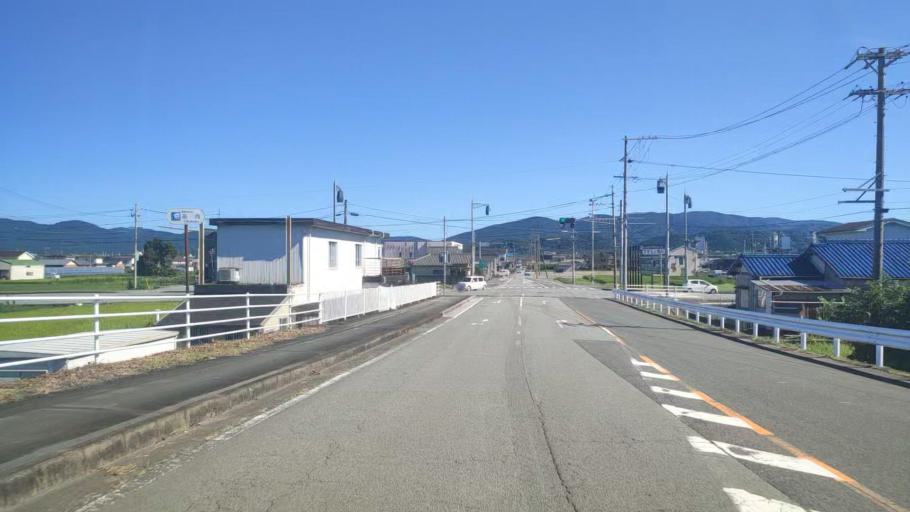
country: JP
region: Mie
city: Ise
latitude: 34.5073
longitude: 136.6948
